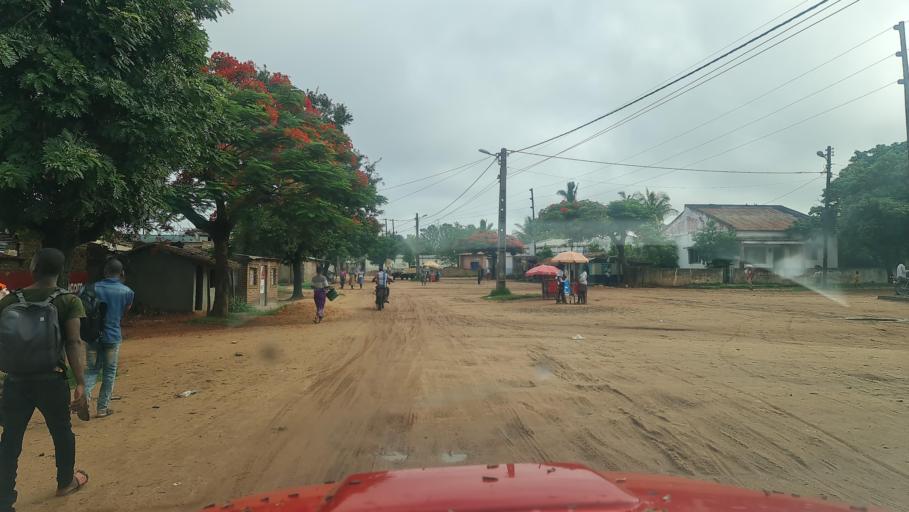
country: MW
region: Southern Region
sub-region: Nsanje District
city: Nsanje
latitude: -17.3269
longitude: 35.5905
